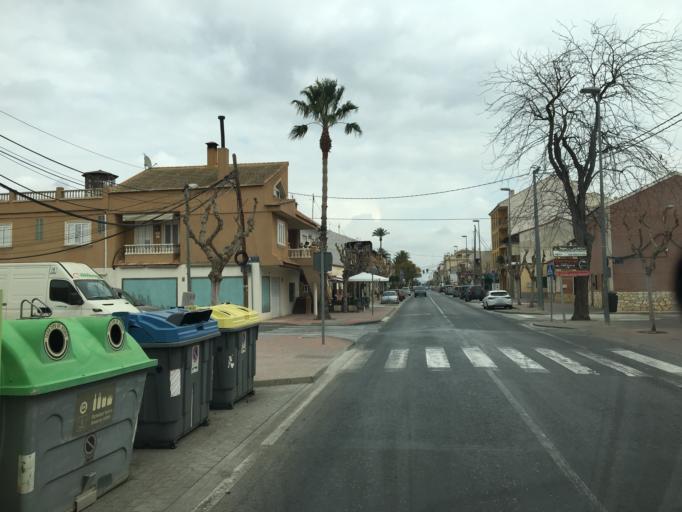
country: ES
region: Murcia
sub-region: Murcia
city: Beniel
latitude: 38.0395
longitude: -1.0291
